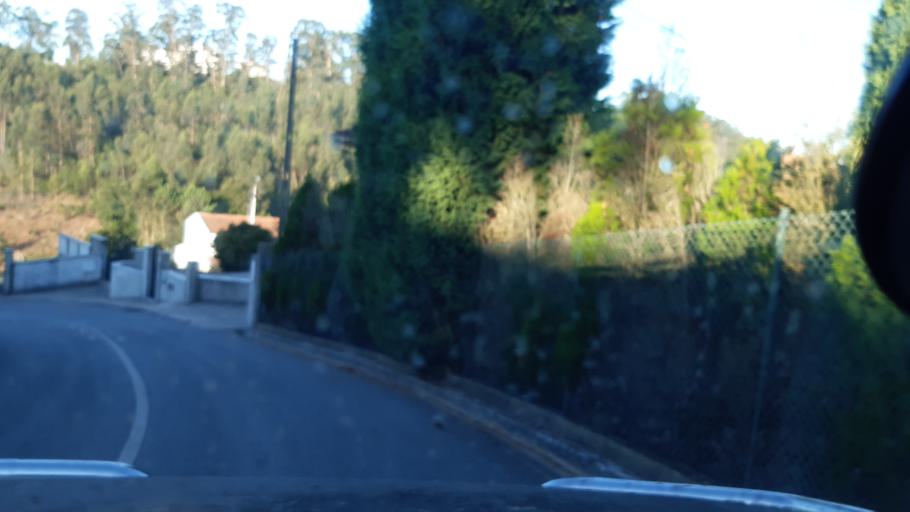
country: PT
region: Aveiro
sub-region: Agueda
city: Agueda
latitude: 40.5804
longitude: -8.4555
